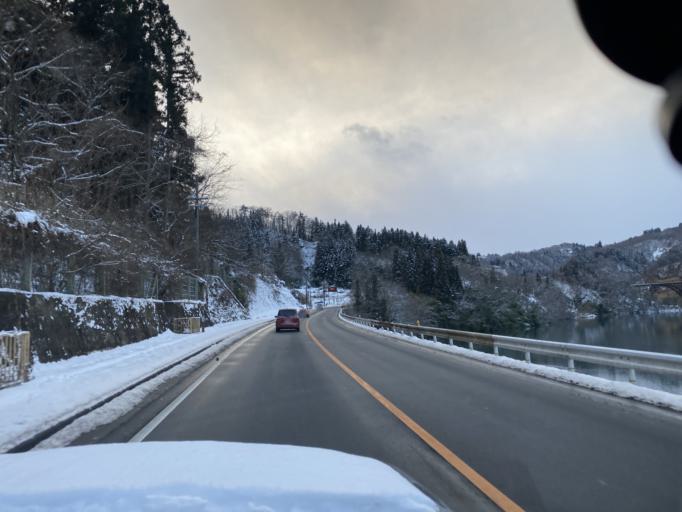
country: JP
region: Nagano
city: Nagano-shi
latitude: 36.5999
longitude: 138.0557
